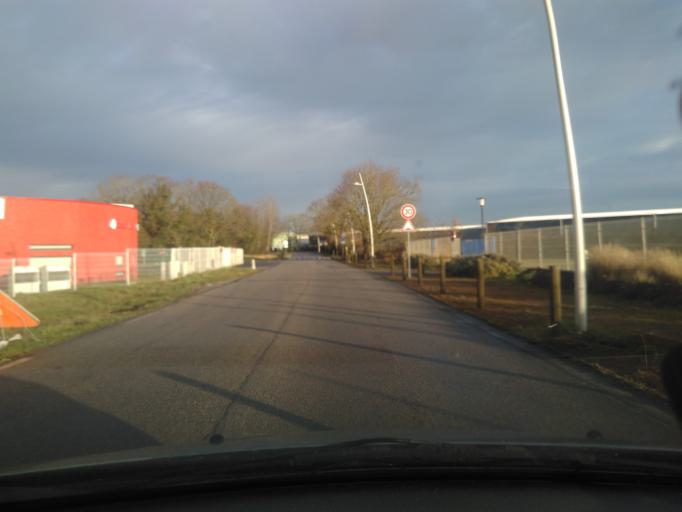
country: FR
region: Pays de la Loire
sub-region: Departement de la Vendee
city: Dompierre-sur-Yon
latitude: 46.6974
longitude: -1.3724
